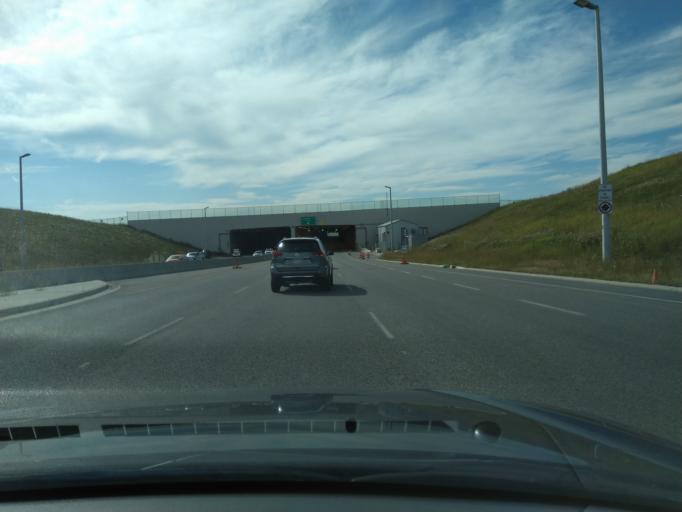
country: CA
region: Alberta
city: Calgary
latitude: 51.1398
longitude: -113.9846
